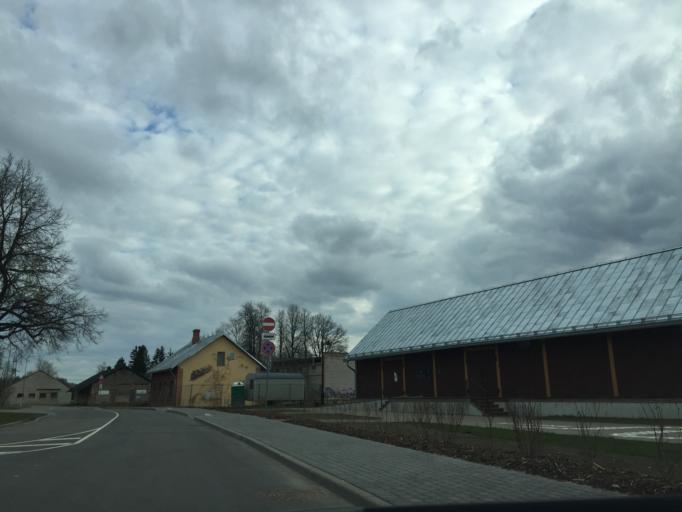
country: LV
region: Aluksnes Rajons
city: Aluksne
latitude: 57.4129
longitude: 27.0456
